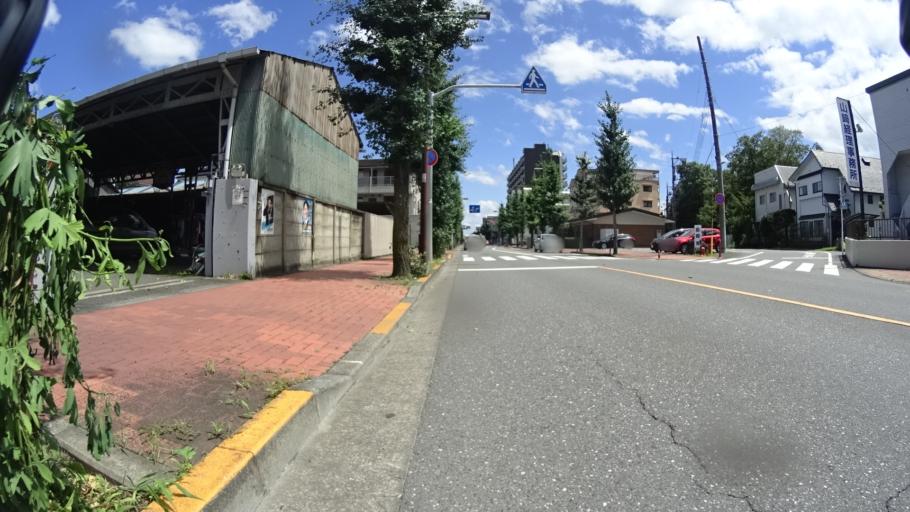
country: JP
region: Tokyo
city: Ome
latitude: 35.7859
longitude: 139.2789
